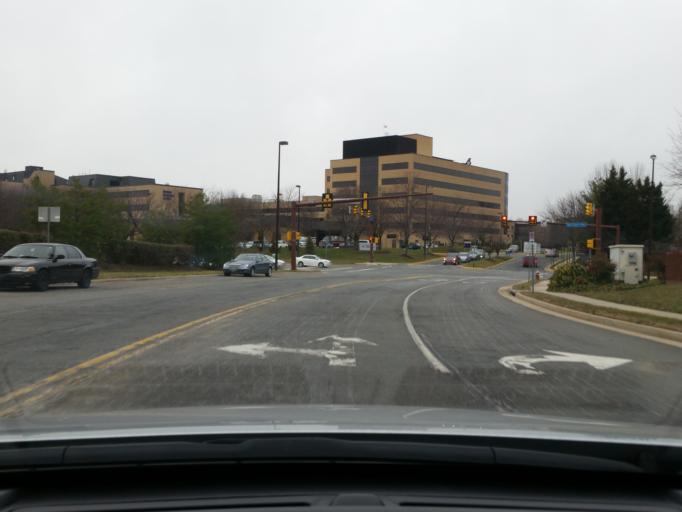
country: US
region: Virginia
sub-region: Fairfax County
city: Reston
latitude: 38.9621
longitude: -77.3612
